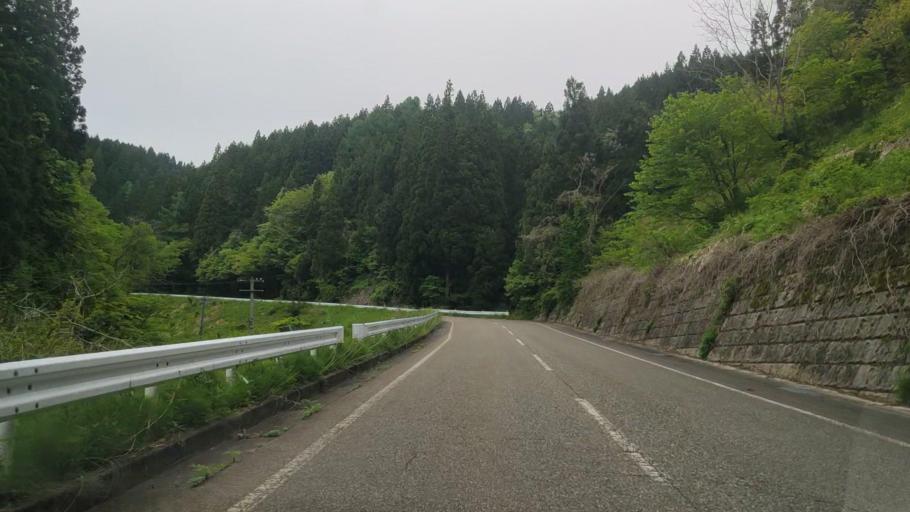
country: JP
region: Niigata
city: Gosen
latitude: 37.7144
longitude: 139.1176
